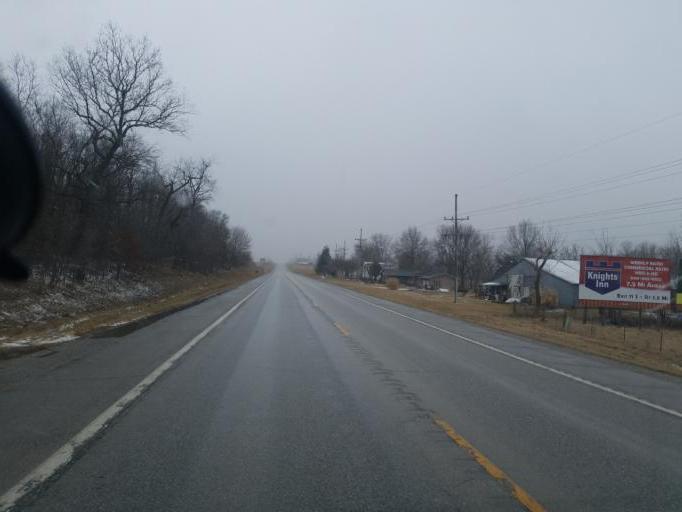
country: US
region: Missouri
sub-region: Adair County
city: Kirksville
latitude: 40.2671
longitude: -92.5825
